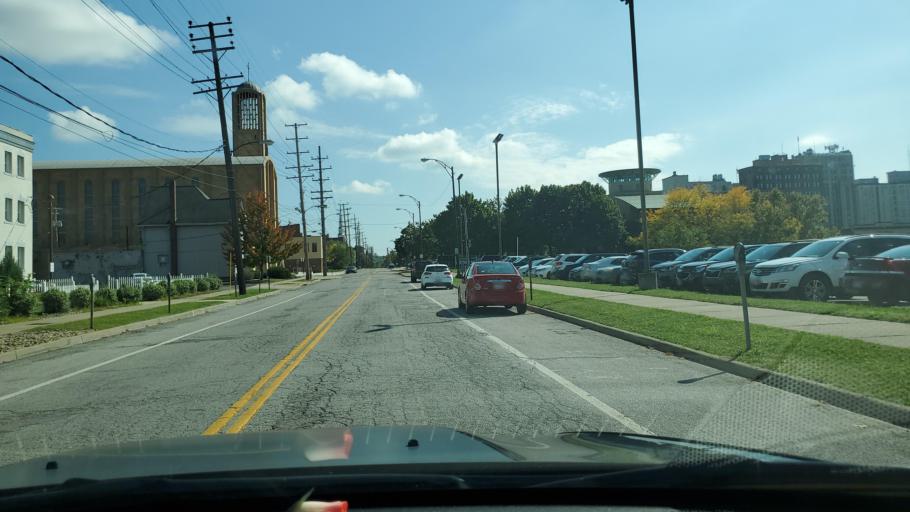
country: US
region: Ohio
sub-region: Mahoning County
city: Youngstown
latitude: 41.1036
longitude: -80.6523
